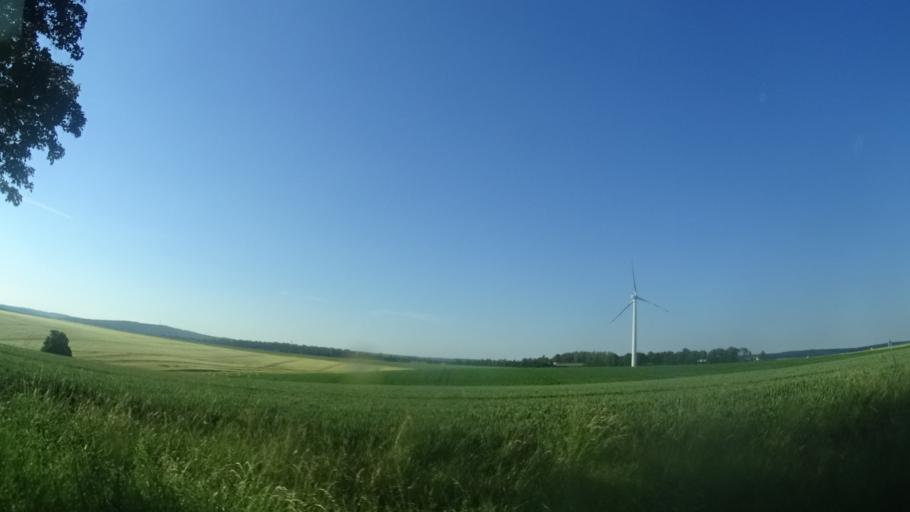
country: DE
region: Lower Saxony
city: Haverlah
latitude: 52.0793
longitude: 10.1788
